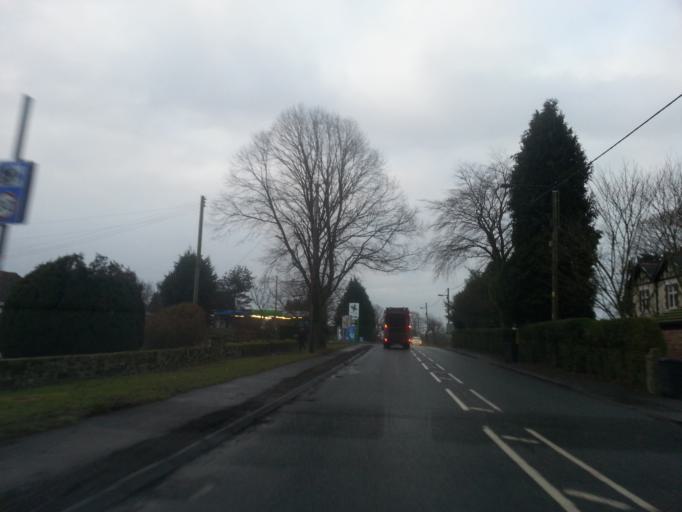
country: GB
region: England
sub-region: County Durham
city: Hamsterley
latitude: 54.7033
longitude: -1.7830
